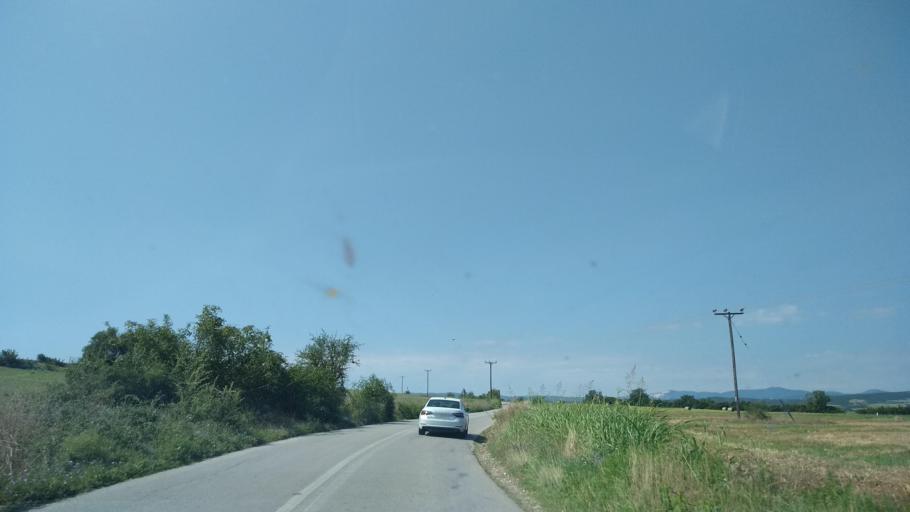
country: GR
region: Central Macedonia
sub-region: Nomos Thessalonikis
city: Nea Apollonia
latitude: 40.6135
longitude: 23.4597
